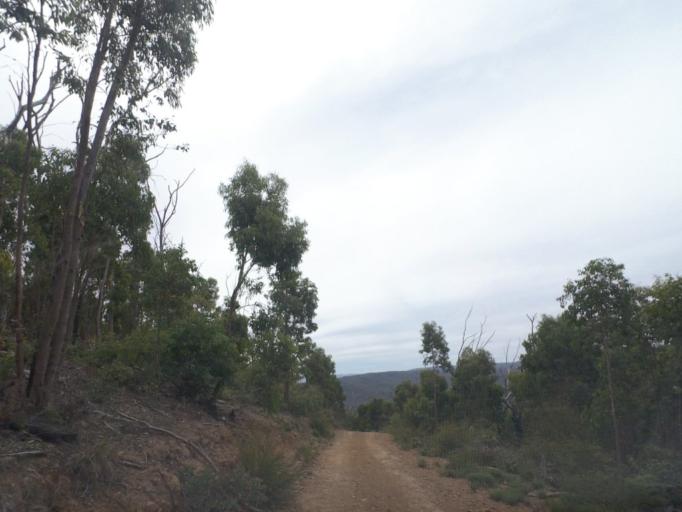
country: AU
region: Victoria
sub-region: Murrindindi
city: Alexandra
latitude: -37.3877
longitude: 145.5700
